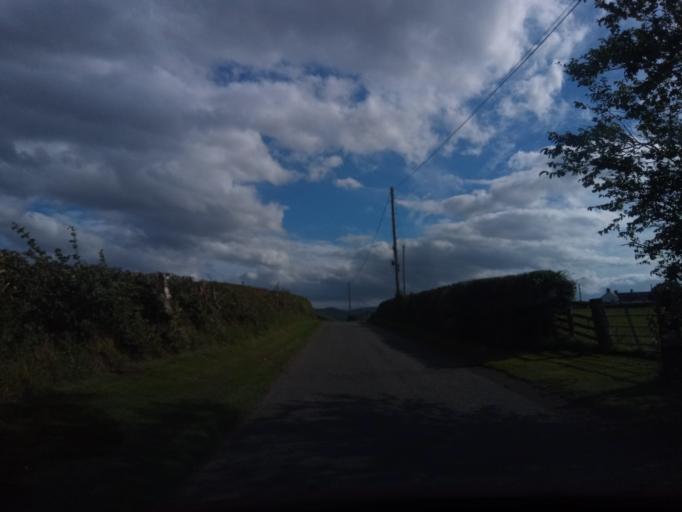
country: GB
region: Scotland
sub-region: The Scottish Borders
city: Coldstream
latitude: 55.5818
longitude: -2.2549
